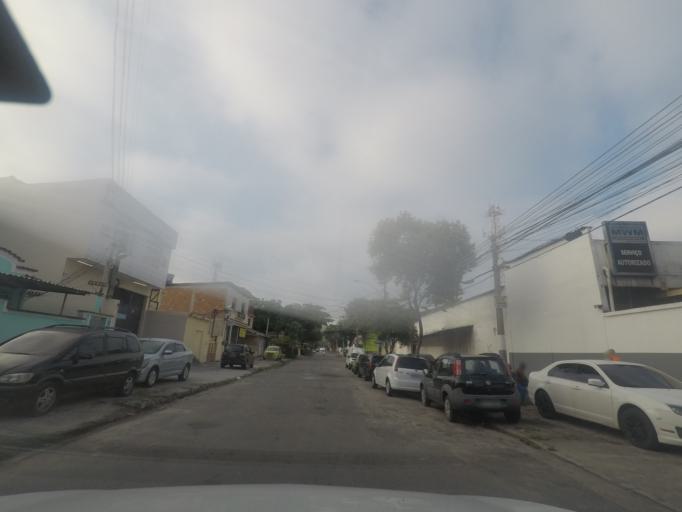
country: BR
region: Rio de Janeiro
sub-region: Duque De Caxias
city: Duque de Caxias
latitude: -22.8340
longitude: -43.2731
